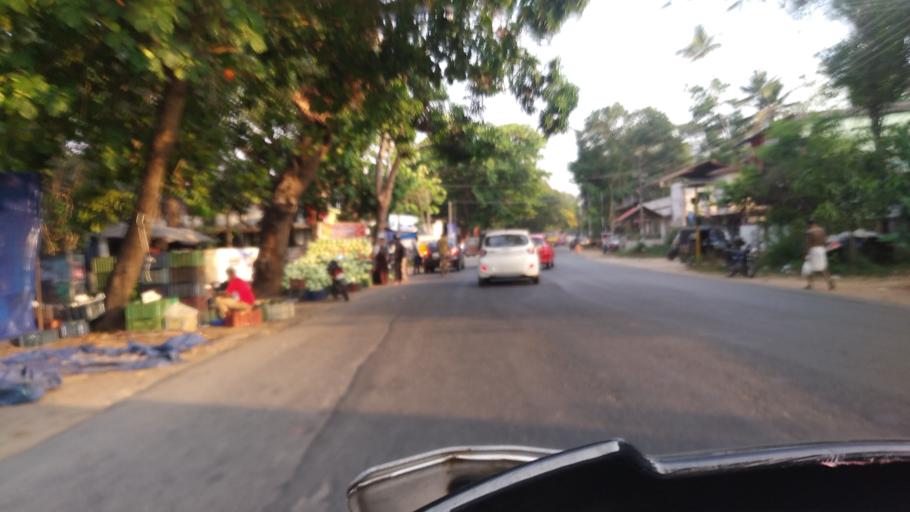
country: IN
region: Kerala
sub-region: Thrissur District
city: Irinjalakuda
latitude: 10.3128
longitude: 76.1491
